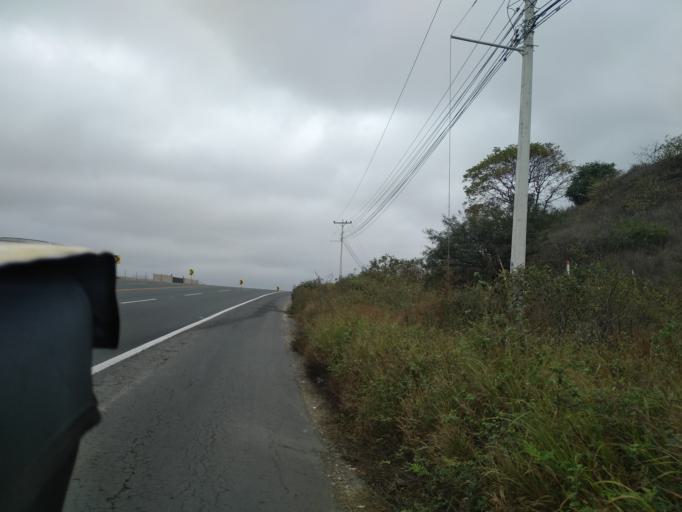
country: EC
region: Santa Elena
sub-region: Canton Santa Elena
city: Santa Elena
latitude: -2.2017
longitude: -80.8539
